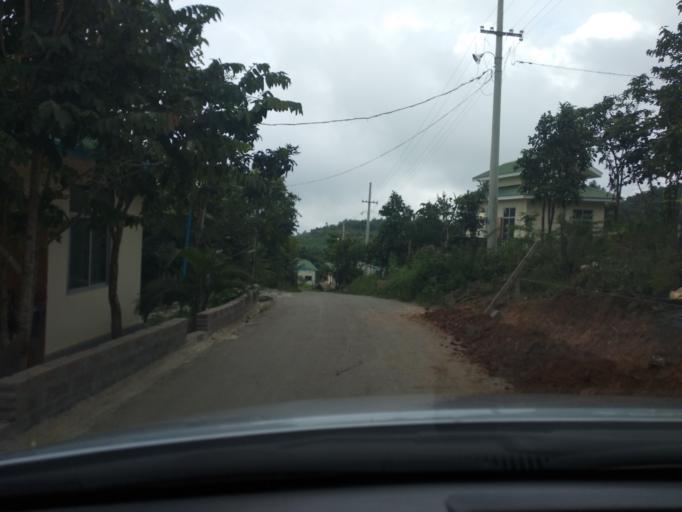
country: MM
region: Mandalay
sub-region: Pyin Oo Lwin District
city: Pyin Oo Lwin
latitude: 21.9158
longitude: 96.3861
